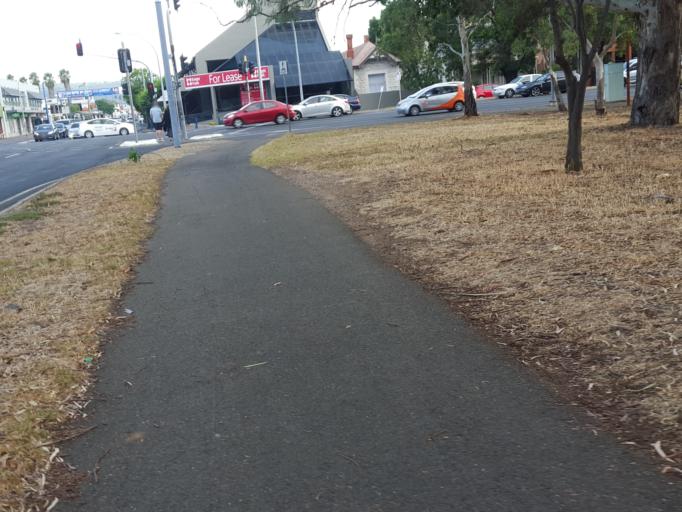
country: AU
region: South Australia
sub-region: Unley
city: Unley
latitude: -34.9404
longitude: 138.6066
